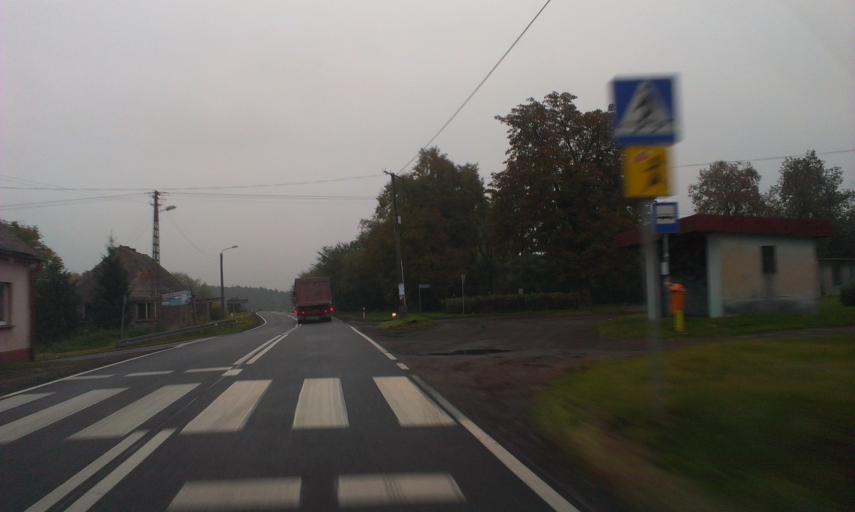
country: PL
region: Kujawsko-Pomorskie
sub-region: Powiat sepolenski
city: Sosno
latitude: 53.4431
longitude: 17.6628
